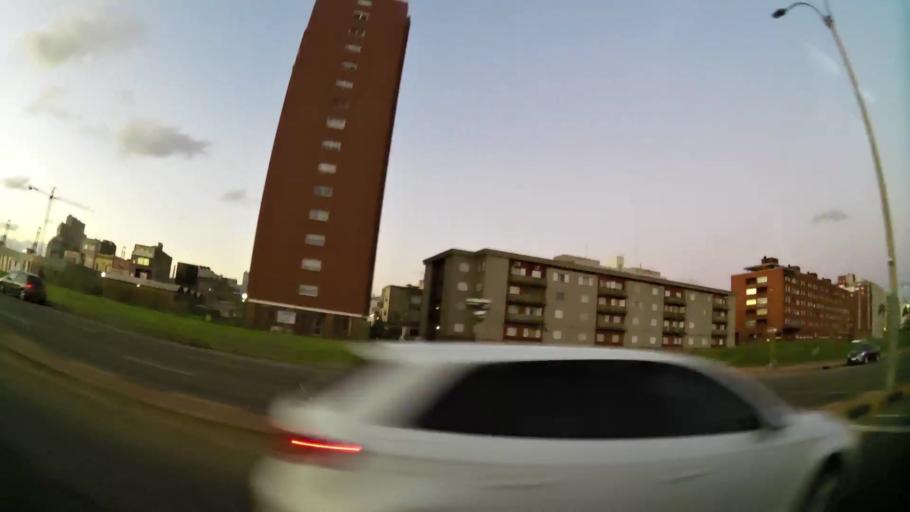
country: UY
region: Montevideo
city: Montevideo
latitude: -34.9119
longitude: -56.2099
